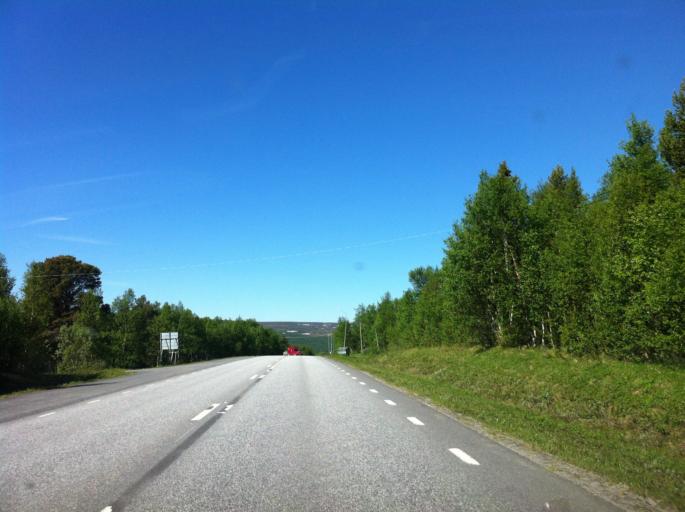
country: NO
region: Hedmark
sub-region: Engerdal
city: Engerdal
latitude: 62.5364
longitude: 12.4054
